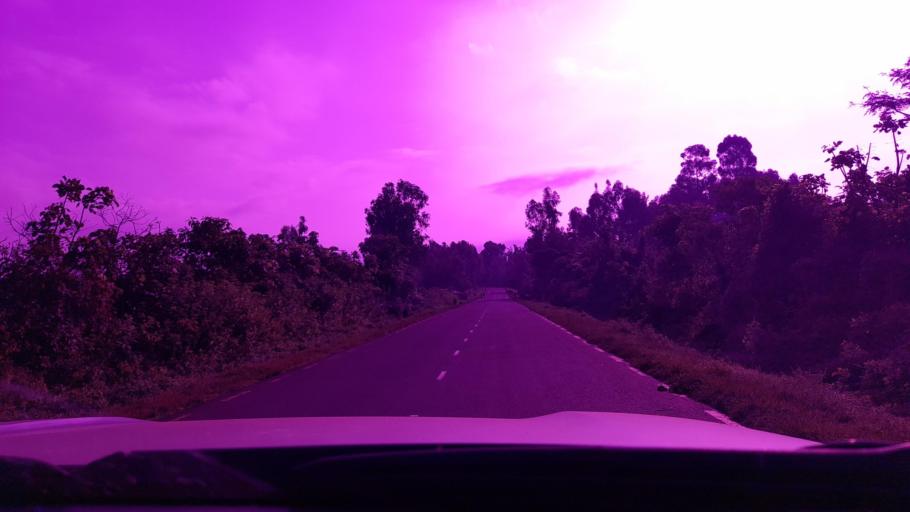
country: ET
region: Oromiya
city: Bedele
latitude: 8.1546
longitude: 36.4716
